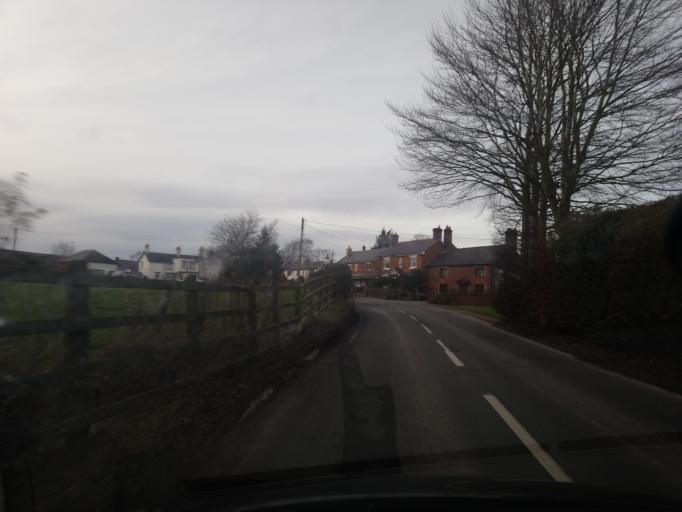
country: GB
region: England
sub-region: Shropshire
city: Whitchurch
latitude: 52.9340
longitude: -2.6824
